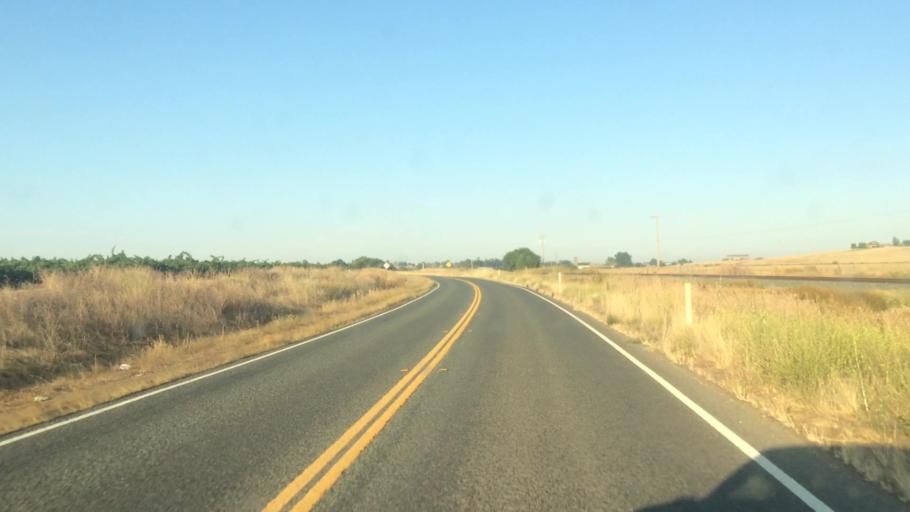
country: US
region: California
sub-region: Sacramento County
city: Clay
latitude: 38.3395
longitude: -121.1443
